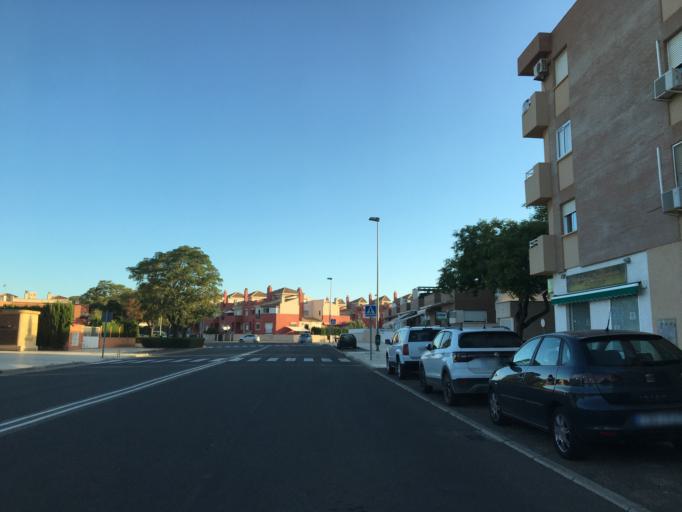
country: ES
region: Murcia
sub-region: Murcia
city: Cartagena
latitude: 37.6524
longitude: -1.0169
